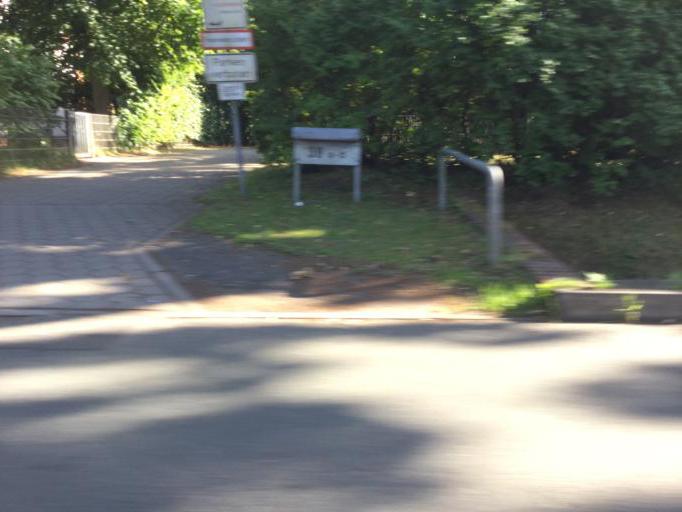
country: DE
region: Hamburg
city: Langenhorn
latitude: 53.6770
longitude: 10.0060
